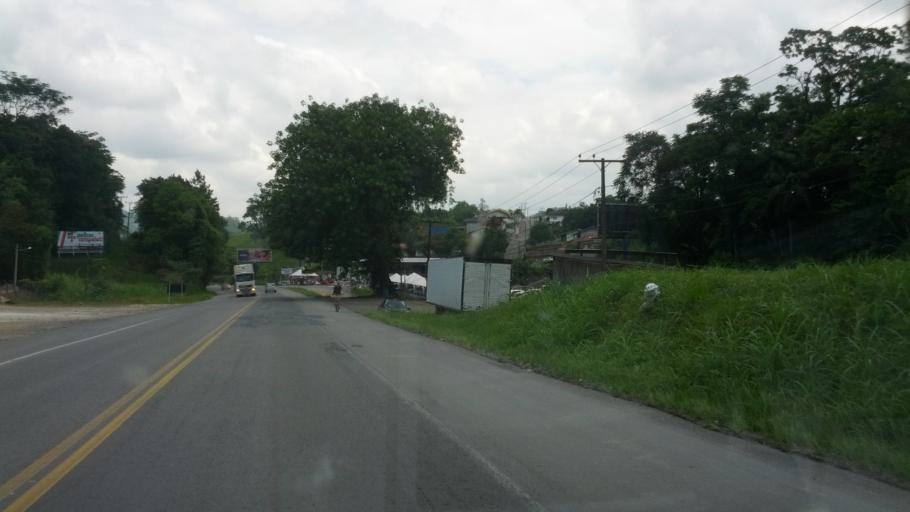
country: BR
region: Santa Catarina
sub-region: Blumenau
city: Blumenau
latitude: -26.8783
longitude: -49.1329
